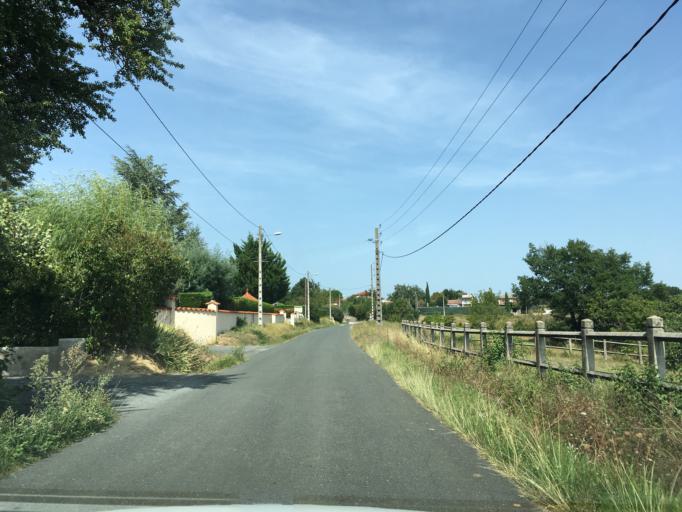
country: FR
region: Midi-Pyrenees
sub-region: Departement du Tarn
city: Castres
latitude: 43.6525
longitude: 2.2348
